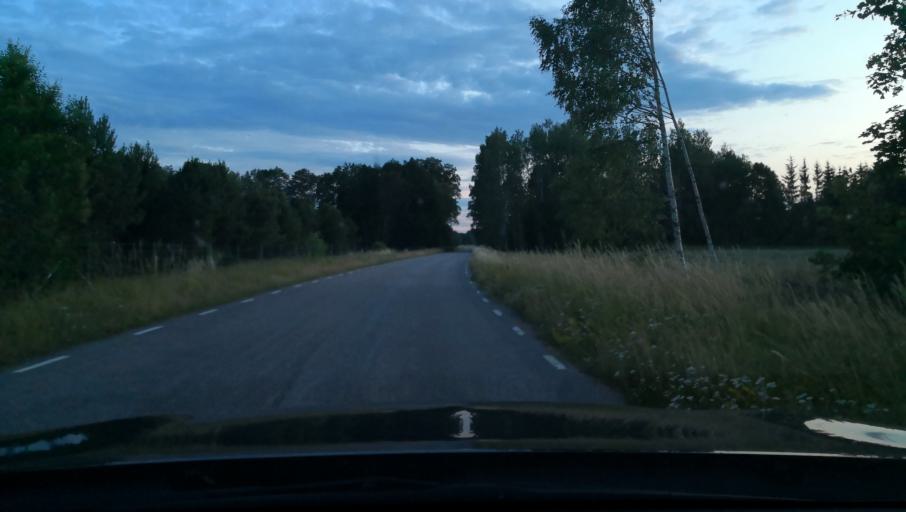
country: SE
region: Uppsala
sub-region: Osthammars Kommun
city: Bjorklinge
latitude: 60.0514
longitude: 17.5238
